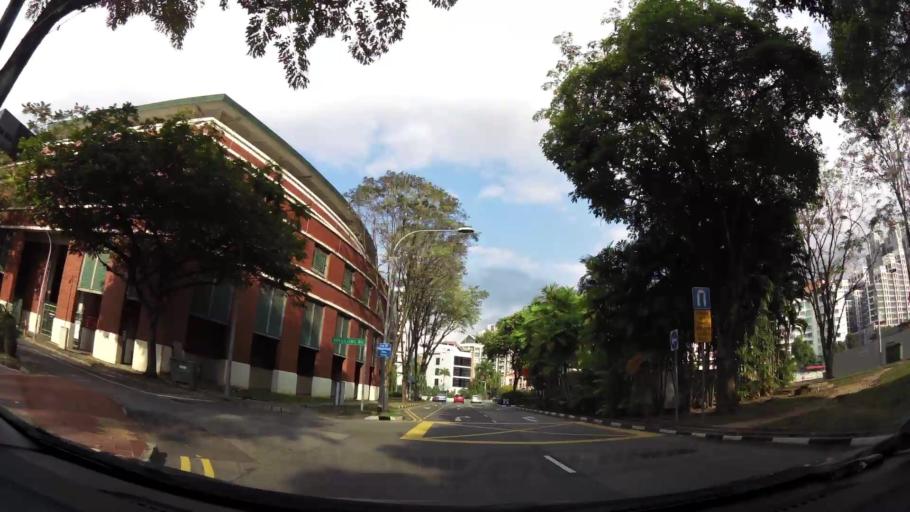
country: SG
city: Singapore
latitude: 1.2895
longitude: 103.8428
